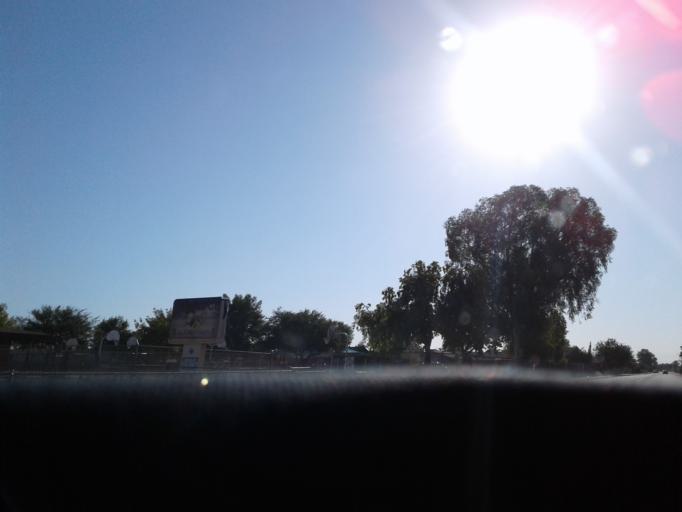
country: US
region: Arizona
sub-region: Maricopa County
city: Tolleson
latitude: 33.4588
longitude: -112.1942
